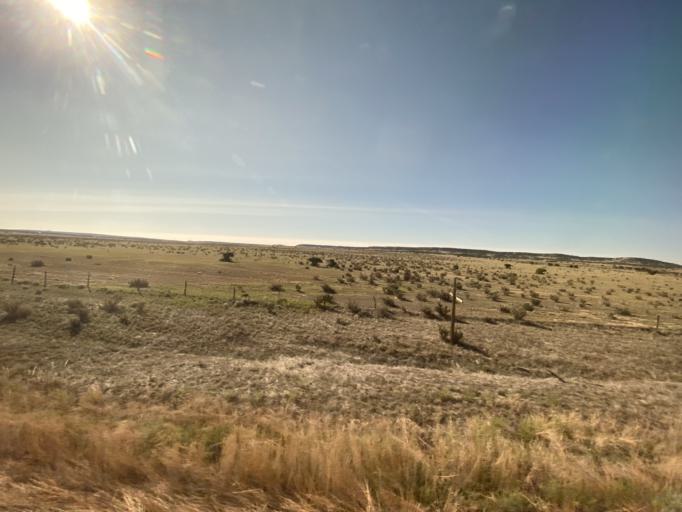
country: US
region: Colorado
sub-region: Otero County
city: Fowler
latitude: 37.5664
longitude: -104.0745
